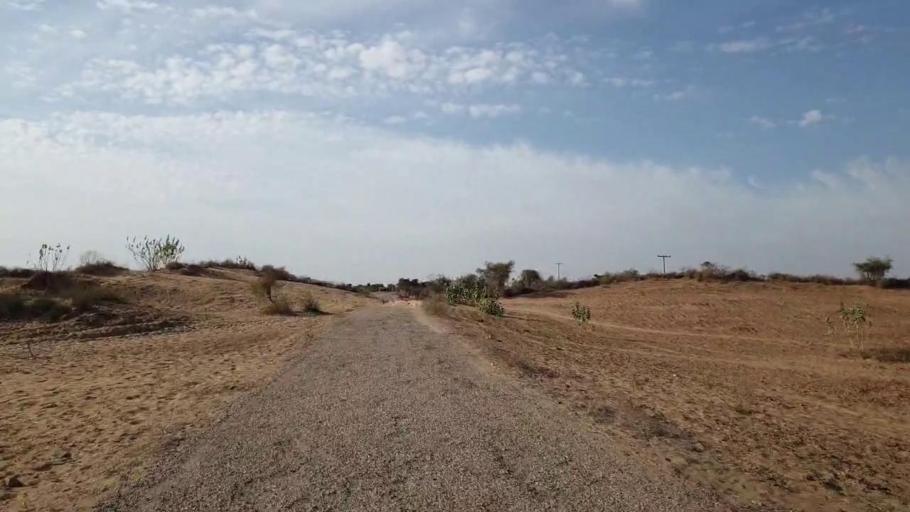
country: PK
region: Sindh
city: Nabisar
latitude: 25.0515
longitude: 69.9688
